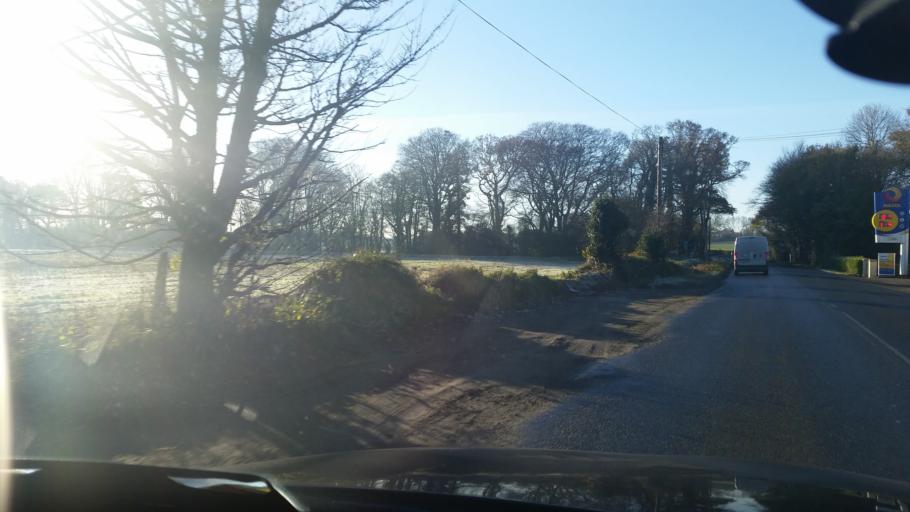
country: IE
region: Leinster
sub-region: Loch Garman
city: Ballinroad
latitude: 52.5379
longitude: -6.3477
